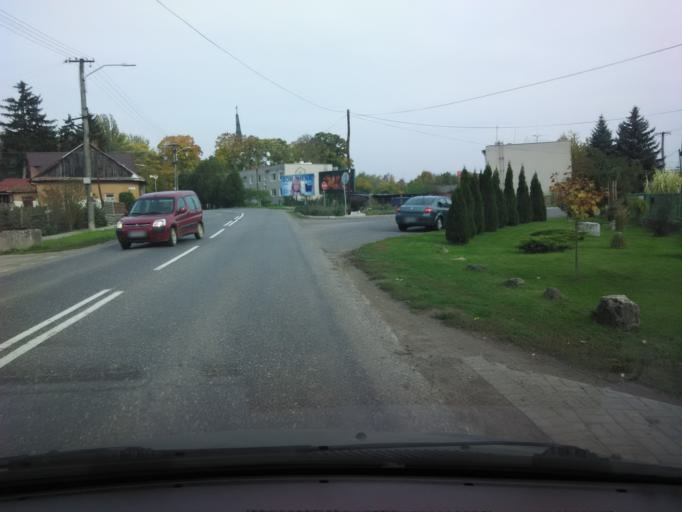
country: SK
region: Nitriansky
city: Levice
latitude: 48.1954
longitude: 18.5161
